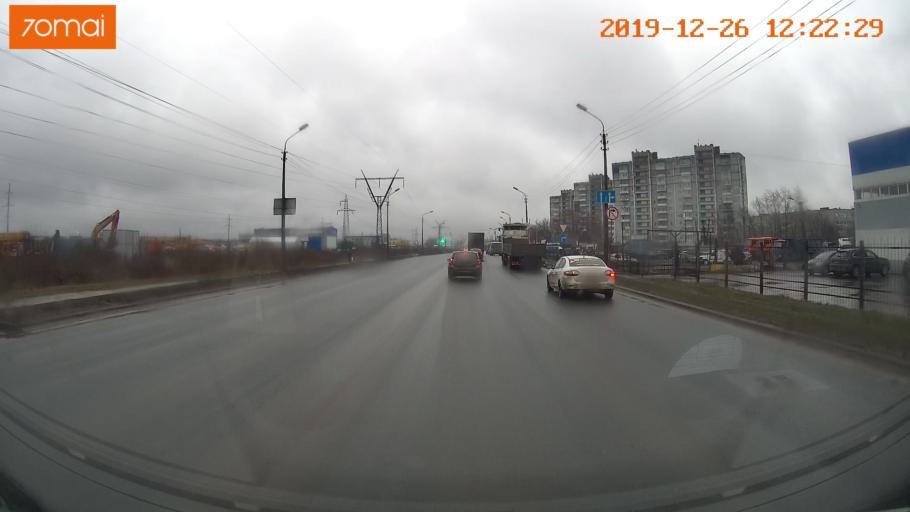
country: RU
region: Vologda
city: Tonshalovo
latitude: 59.1505
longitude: 37.9467
